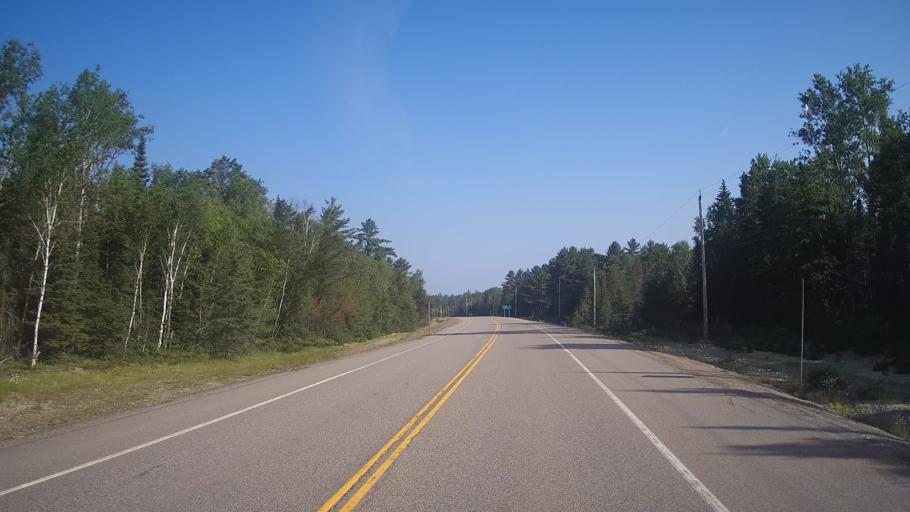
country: CA
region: Ontario
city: Rayside-Balfour
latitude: 46.7348
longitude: -81.5917
